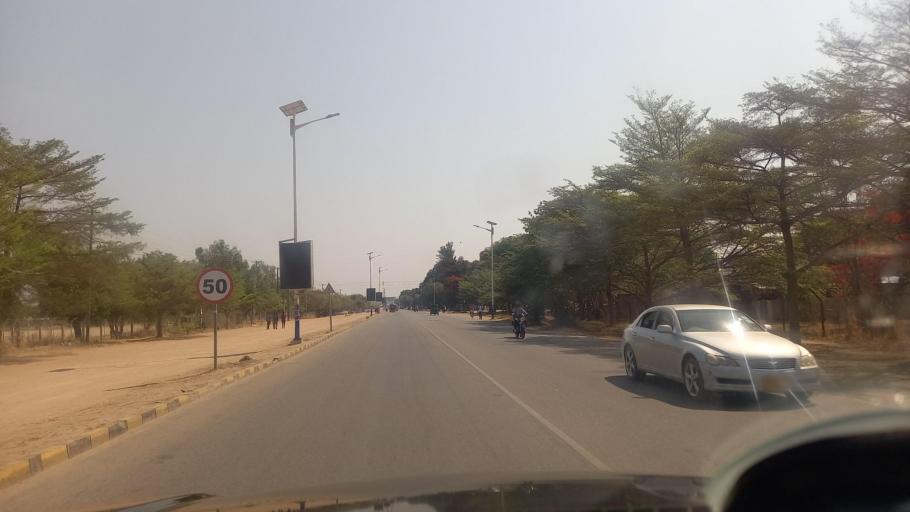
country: TZ
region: Dodoma
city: Dodoma
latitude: -6.1805
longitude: 35.7539
